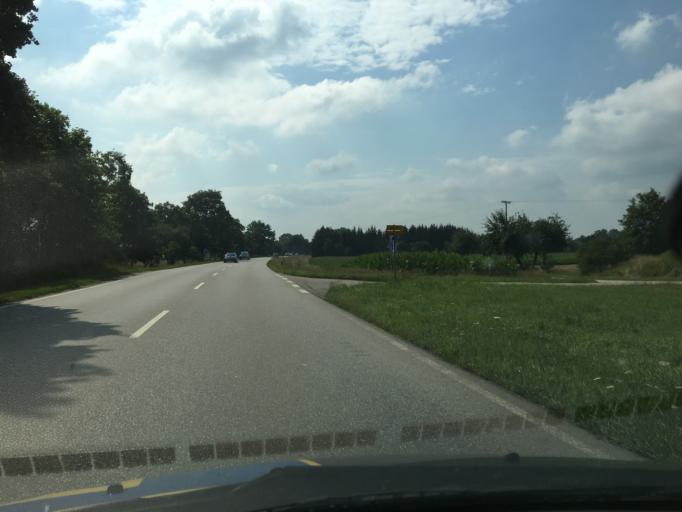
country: DE
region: Bavaria
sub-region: Upper Bavaria
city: Winhoring
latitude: 48.2613
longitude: 12.6598
